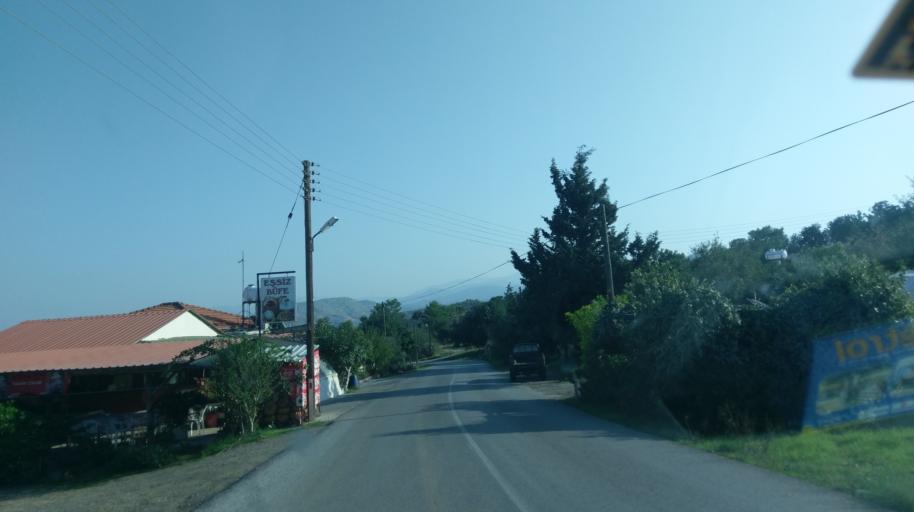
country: CY
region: Lefkosia
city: Kato Pyrgos
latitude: 35.1595
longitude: 32.7632
